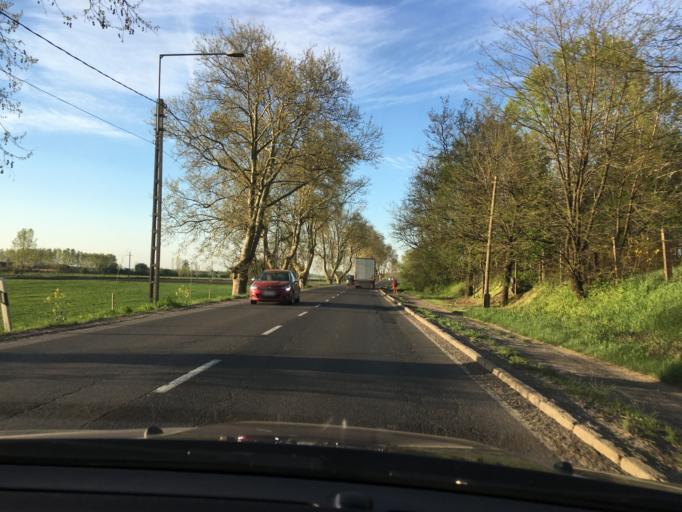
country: HU
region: Hajdu-Bihar
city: Mikepercs
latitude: 47.4307
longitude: 21.6266
